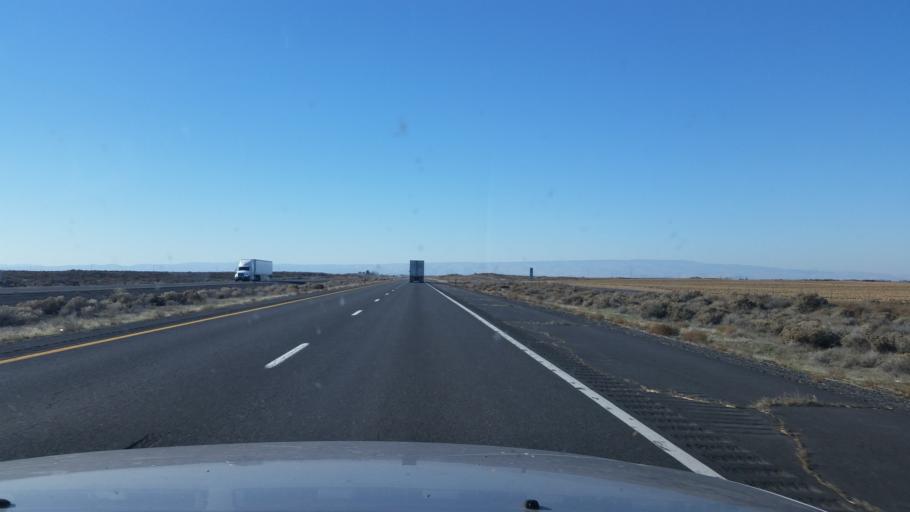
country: US
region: Washington
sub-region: Grant County
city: Quincy
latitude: 47.1038
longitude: -119.6959
